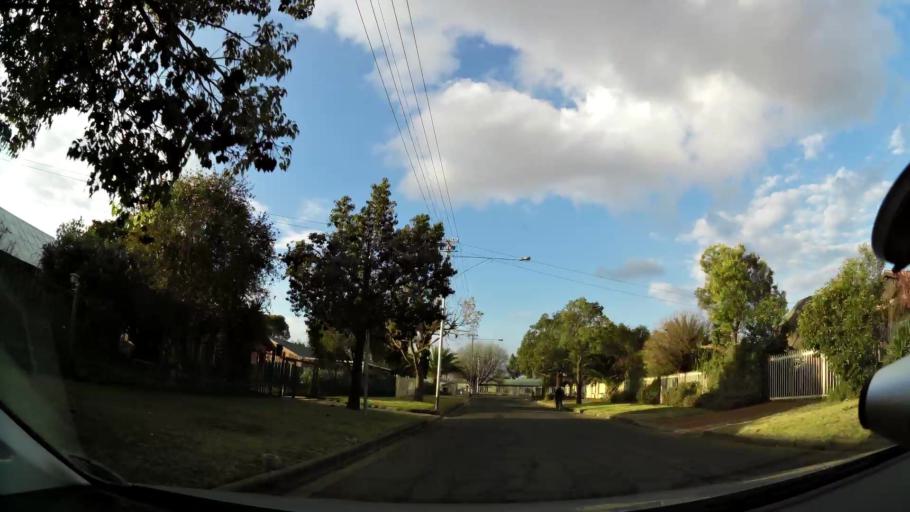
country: ZA
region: Orange Free State
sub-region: Mangaung Metropolitan Municipality
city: Bloemfontein
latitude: -29.1416
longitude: 26.1958
